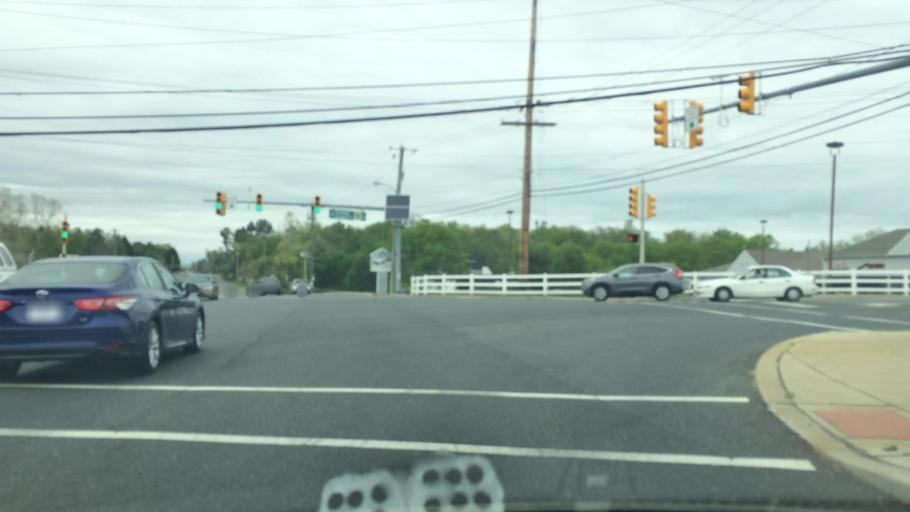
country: US
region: New Jersey
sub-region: Gloucester County
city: Turnersville
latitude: 39.7647
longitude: -75.0856
